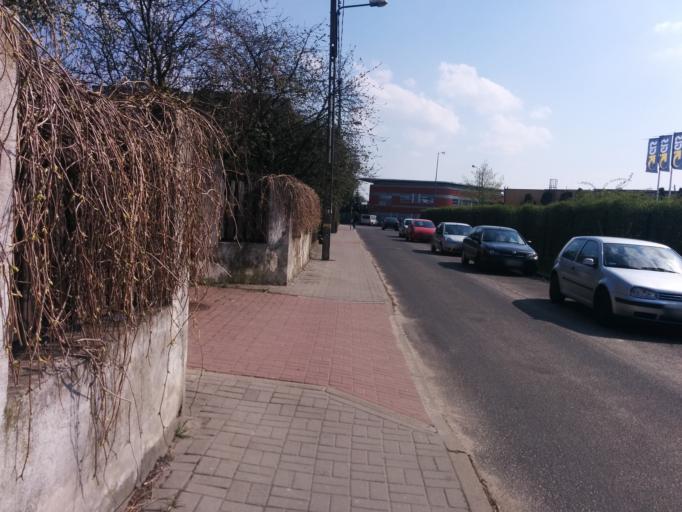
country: PL
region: Masovian Voivodeship
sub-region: Warszawa
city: Wlochy
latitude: 52.1954
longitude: 20.9530
